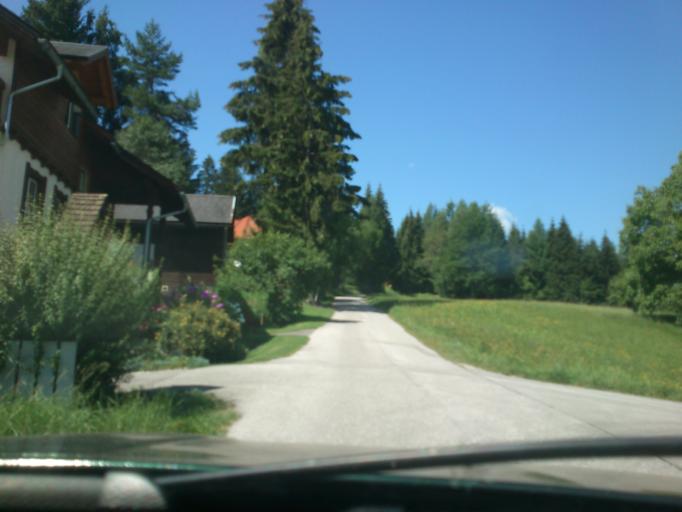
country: AT
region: Upper Austria
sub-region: Politischer Bezirk Kirchdorf an der Krems
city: Rossleithen
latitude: 47.7265
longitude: 14.3506
